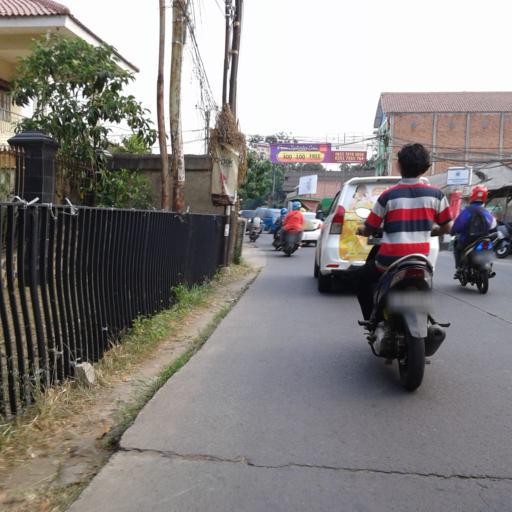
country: ID
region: West Java
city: Sawangan
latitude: -6.3843
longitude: 106.7687
